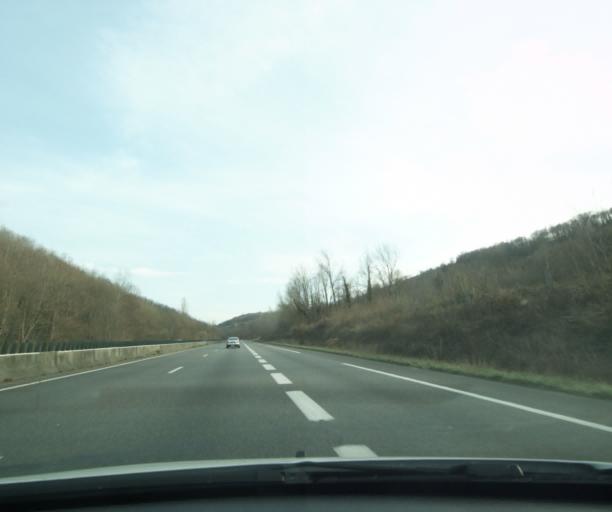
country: FR
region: Midi-Pyrenees
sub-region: Departement des Hautes-Pyrenees
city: Tournay
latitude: 43.1550
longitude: 0.2907
